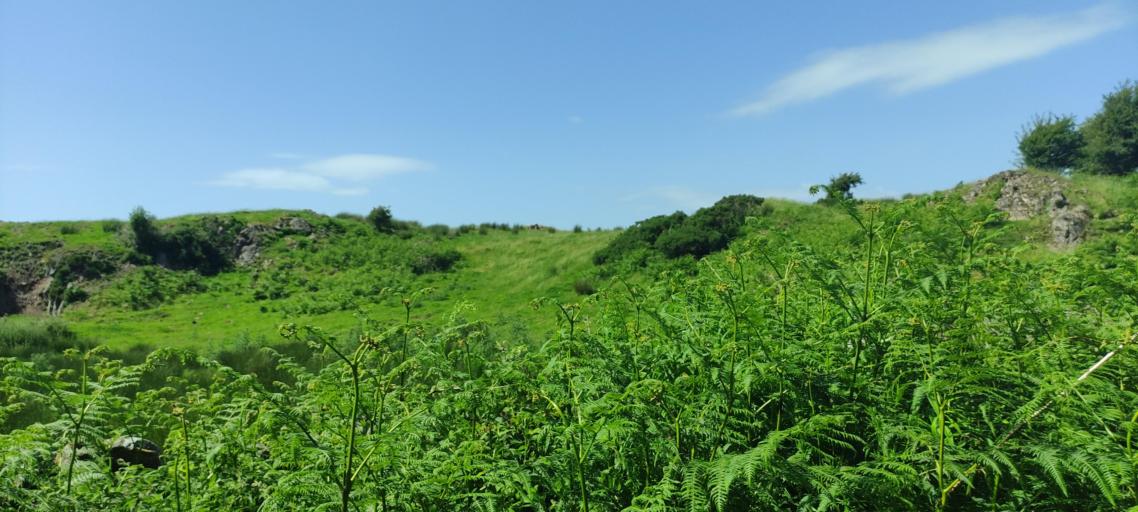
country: GB
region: England
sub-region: Cumbria
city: Seascale
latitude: 54.3625
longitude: -3.3813
